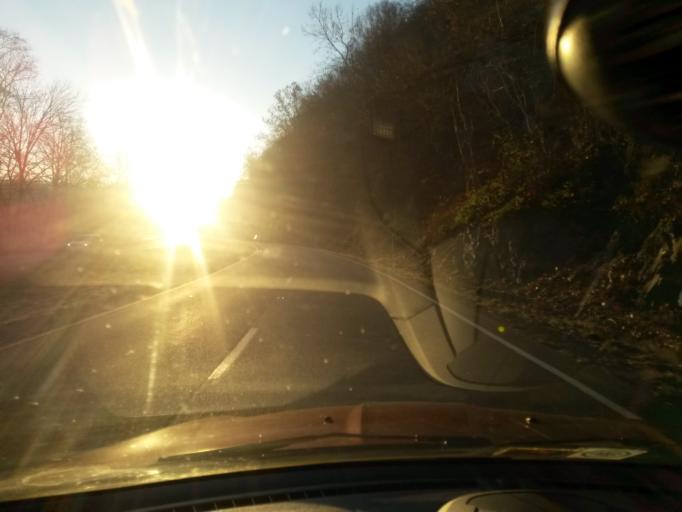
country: US
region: Virginia
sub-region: City of Buena Vista
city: Buena Vista
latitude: 37.7504
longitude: -79.3912
